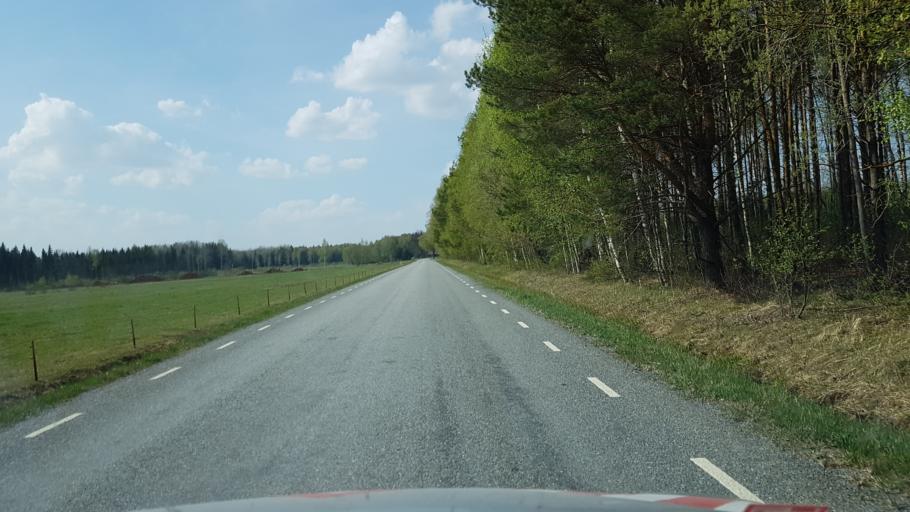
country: EE
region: Paernumaa
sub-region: Paikuse vald
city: Paikuse
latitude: 58.4365
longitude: 24.6163
